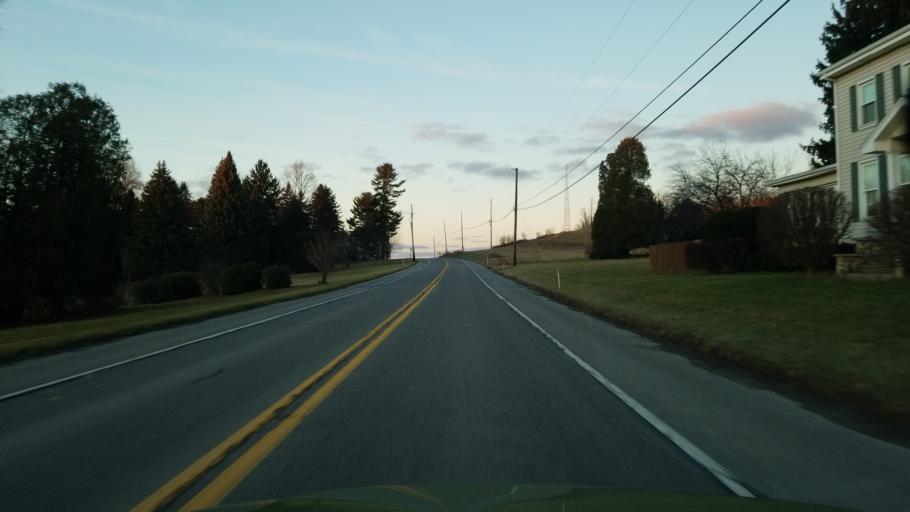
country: US
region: Pennsylvania
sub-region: Jefferson County
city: Punxsutawney
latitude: 40.8709
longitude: -79.0203
